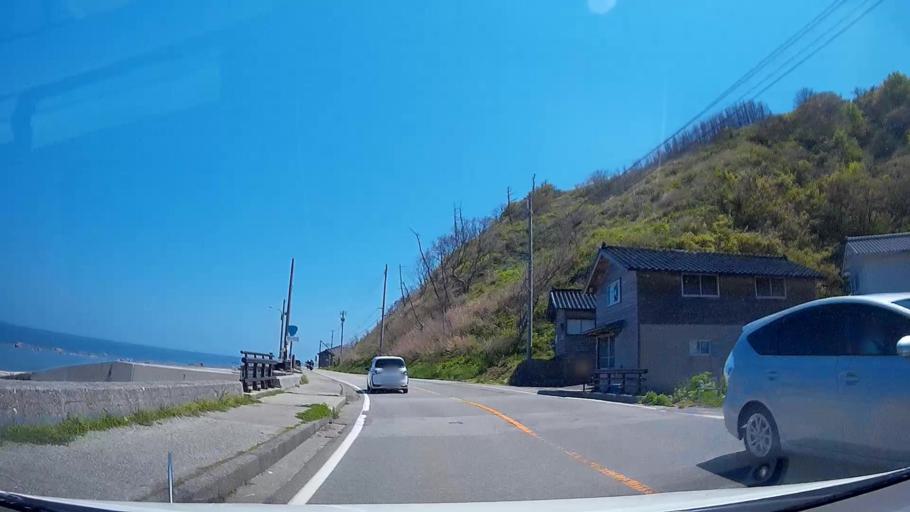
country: JP
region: Ishikawa
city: Nanao
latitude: 37.4311
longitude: 137.0133
